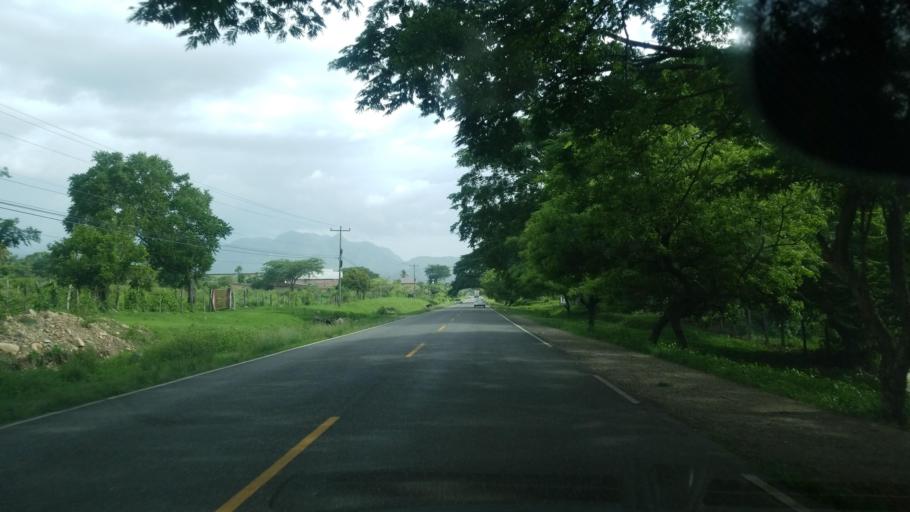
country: HN
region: Ocotepeque
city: Antigua Ocotepeque
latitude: 14.3995
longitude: -89.1977
